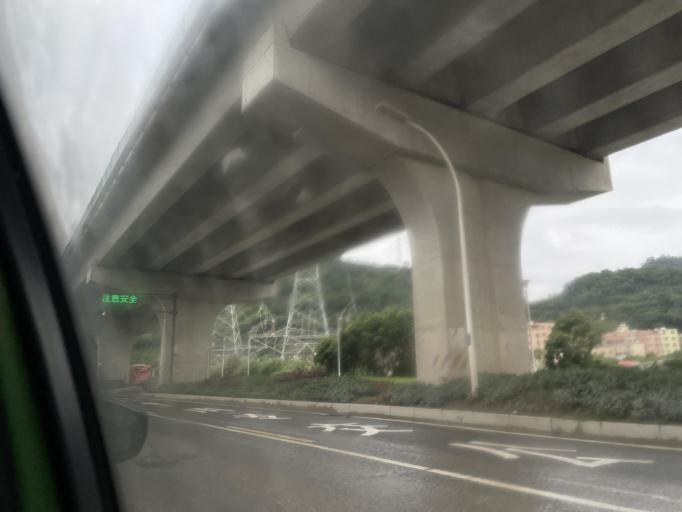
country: CN
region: Guangdong
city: Nanping
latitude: 22.1765
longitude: 113.4731
